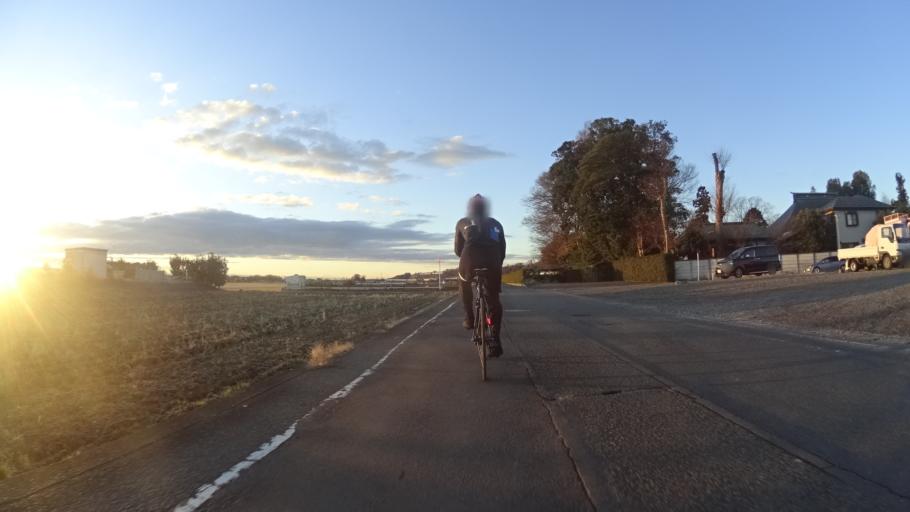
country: JP
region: Kanagawa
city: Zama
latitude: 35.5145
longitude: 139.3685
